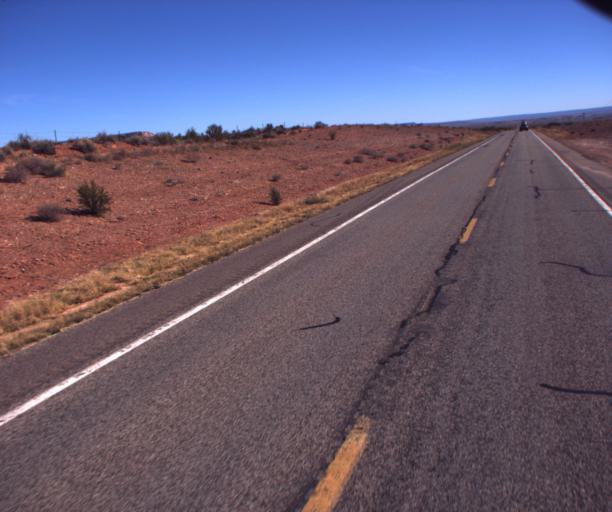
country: US
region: Arizona
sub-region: Coconino County
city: Fredonia
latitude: 36.8721
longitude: -112.6758
